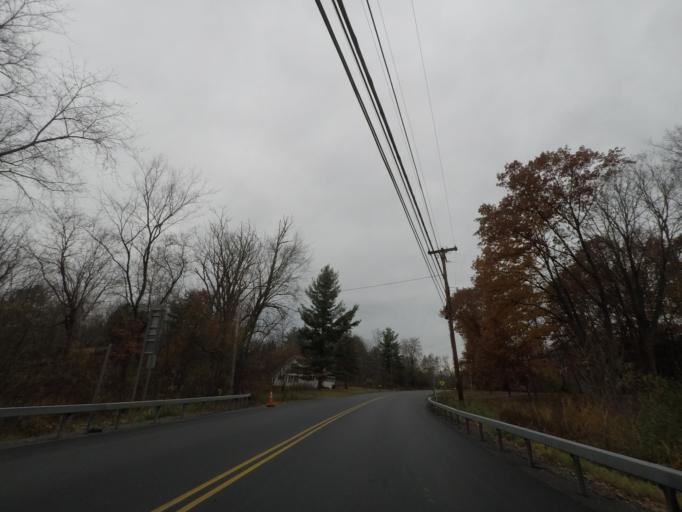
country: US
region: New York
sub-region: Saratoga County
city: Waterford
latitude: 42.8395
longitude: -73.6745
